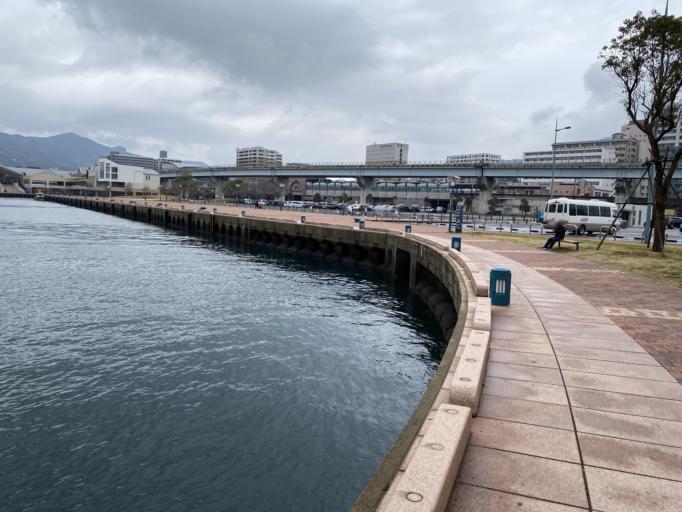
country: JP
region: Nagasaki
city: Sasebo
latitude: 33.1614
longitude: 129.7259
